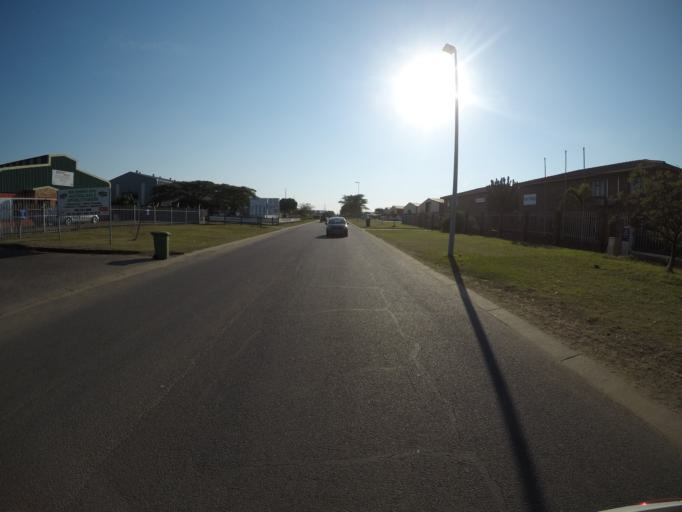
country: ZA
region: KwaZulu-Natal
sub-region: uThungulu District Municipality
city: Richards Bay
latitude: -28.7431
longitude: 32.0366
